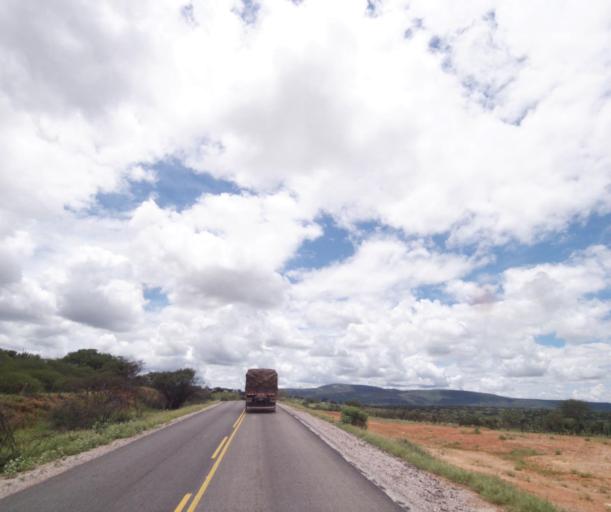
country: BR
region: Bahia
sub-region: Brumado
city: Brumado
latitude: -14.1511
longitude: -41.5066
